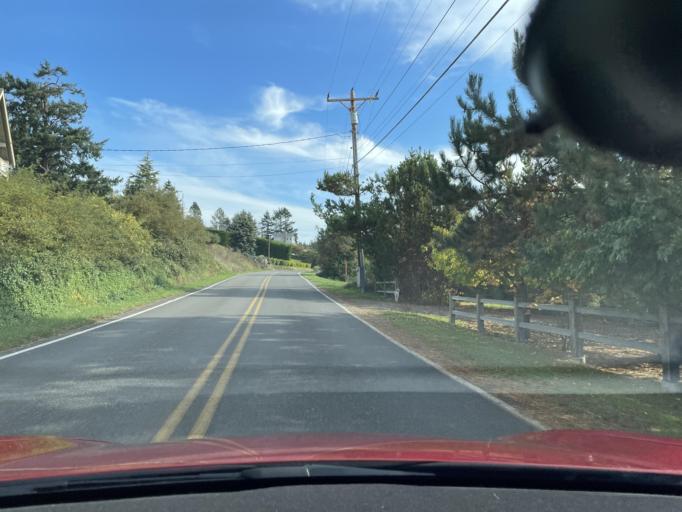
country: US
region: Washington
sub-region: San Juan County
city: Friday Harbor
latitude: 48.5223
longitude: -123.0127
